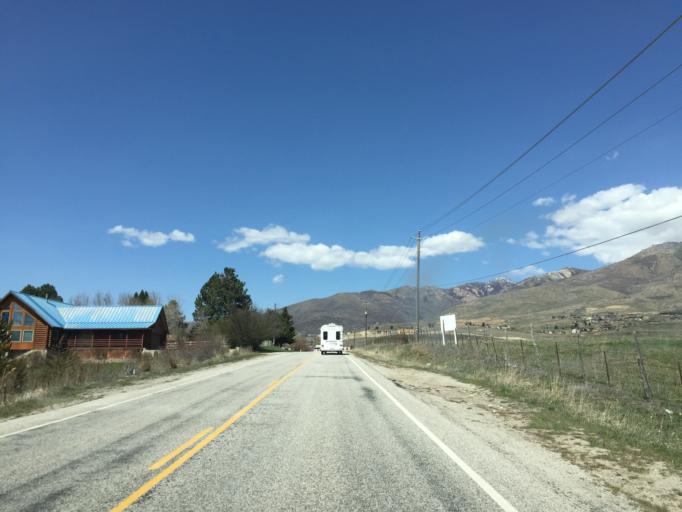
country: US
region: Utah
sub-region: Weber County
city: Wolf Creek
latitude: 41.3093
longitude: -111.8252
